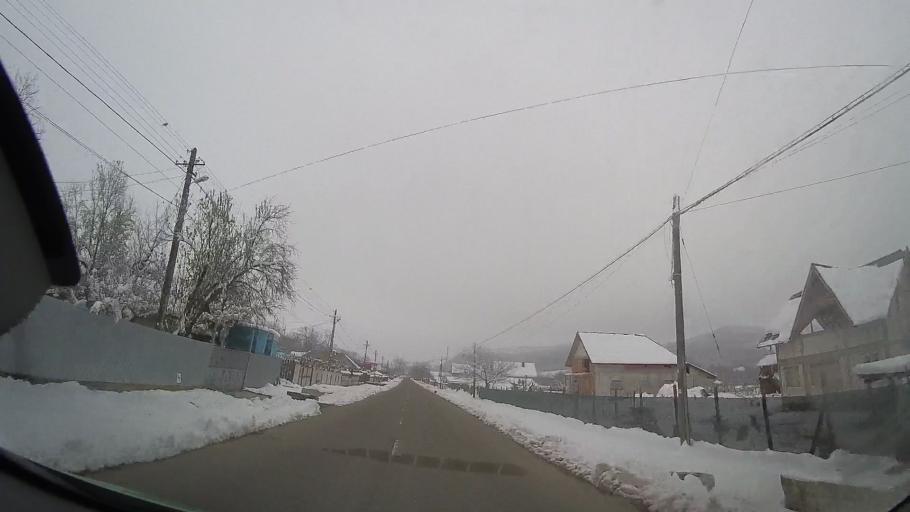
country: RO
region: Neamt
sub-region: Comuna Bozieni
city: Bozieni
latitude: 46.8371
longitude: 27.1542
